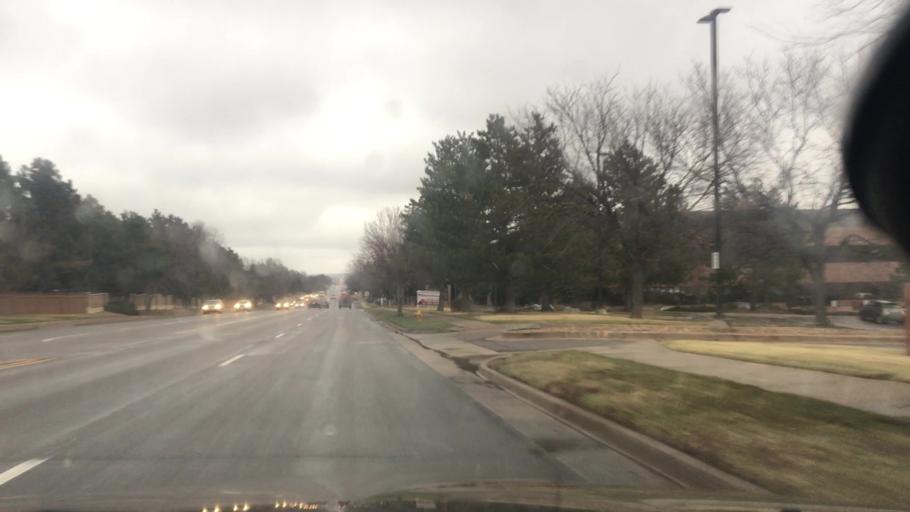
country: US
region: Colorado
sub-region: Arapahoe County
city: Castlewood
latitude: 39.5692
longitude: -104.9230
